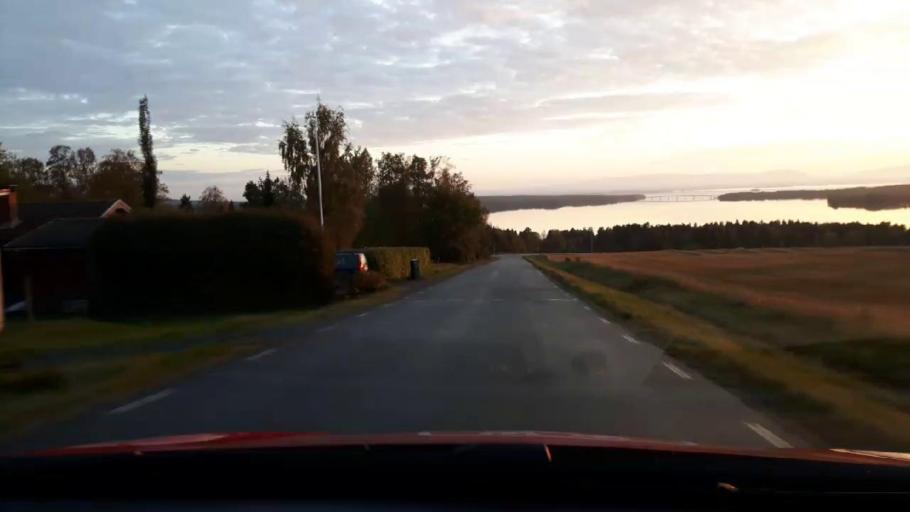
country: SE
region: Jaemtland
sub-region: OEstersunds Kommun
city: Ostersund
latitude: 63.2449
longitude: 14.5470
